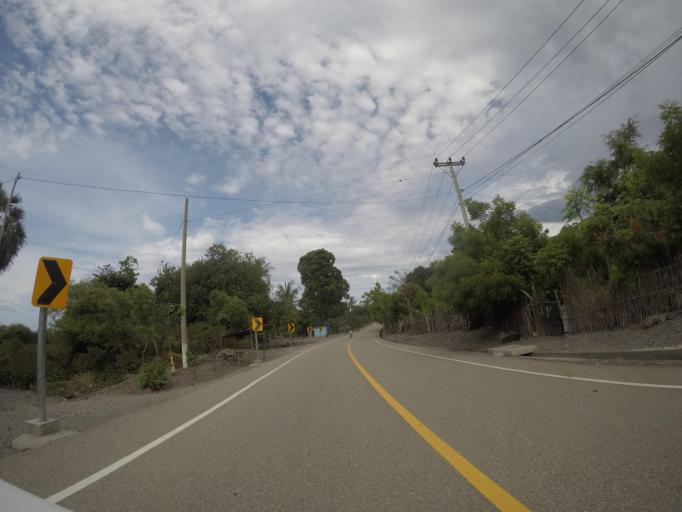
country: TL
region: Liquica
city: Maubara
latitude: -8.6205
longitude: 125.1719
